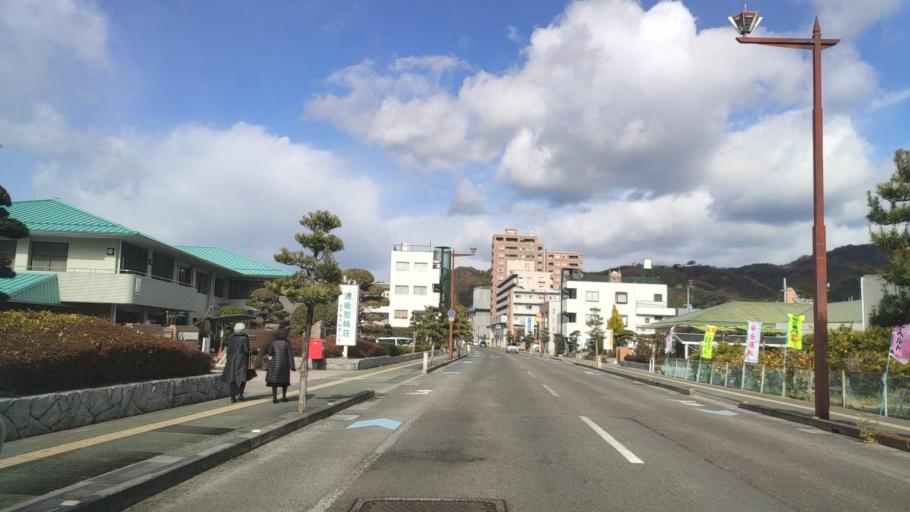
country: JP
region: Ehime
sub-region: Shikoku-chuo Shi
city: Matsuyama
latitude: 33.8497
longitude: 132.7807
